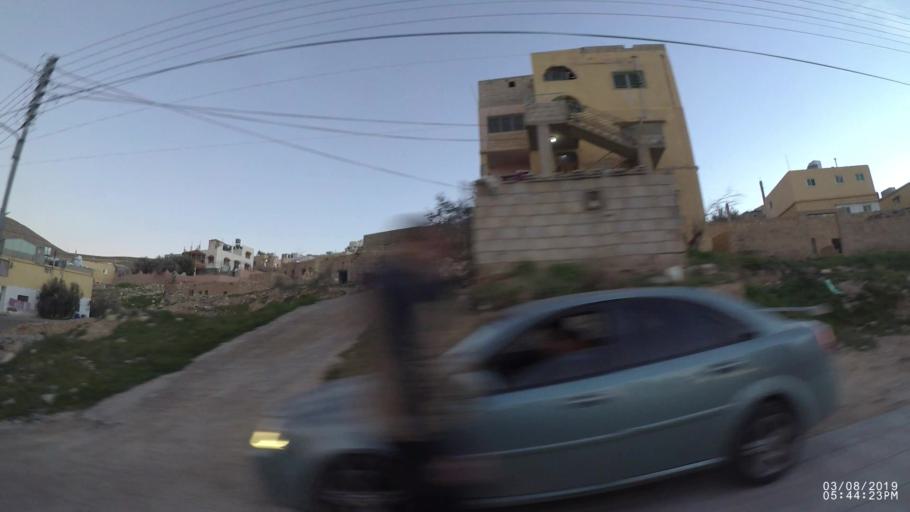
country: JO
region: Ma'an
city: Petra
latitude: 30.3116
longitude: 35.4819
